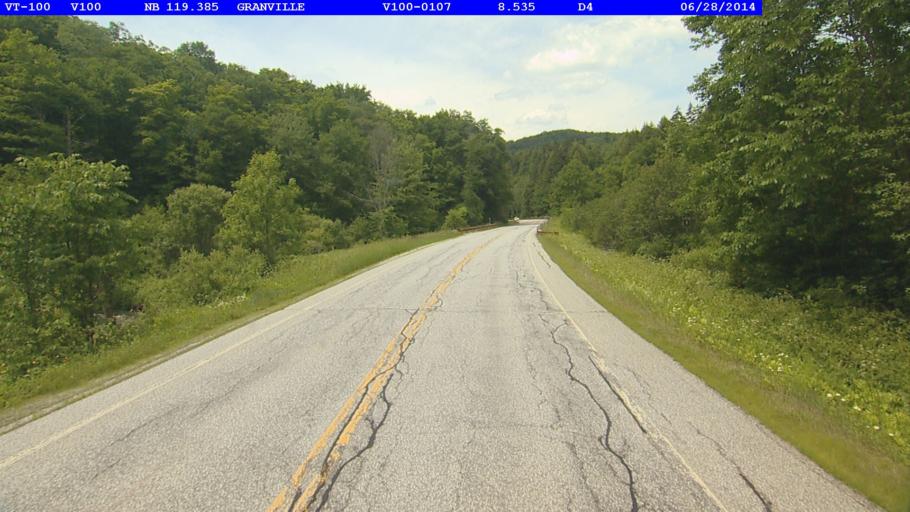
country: US
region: Vermont
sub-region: Washington County
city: Northfield
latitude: 44.0522
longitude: -72.8335
